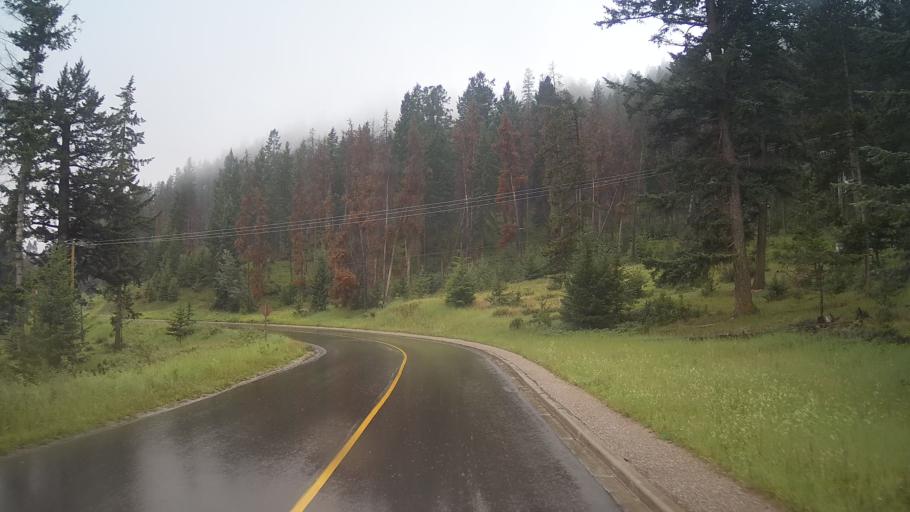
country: CA
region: Alberta
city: Jasper Park Lodge
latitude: 52.8844
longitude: -118.0856
